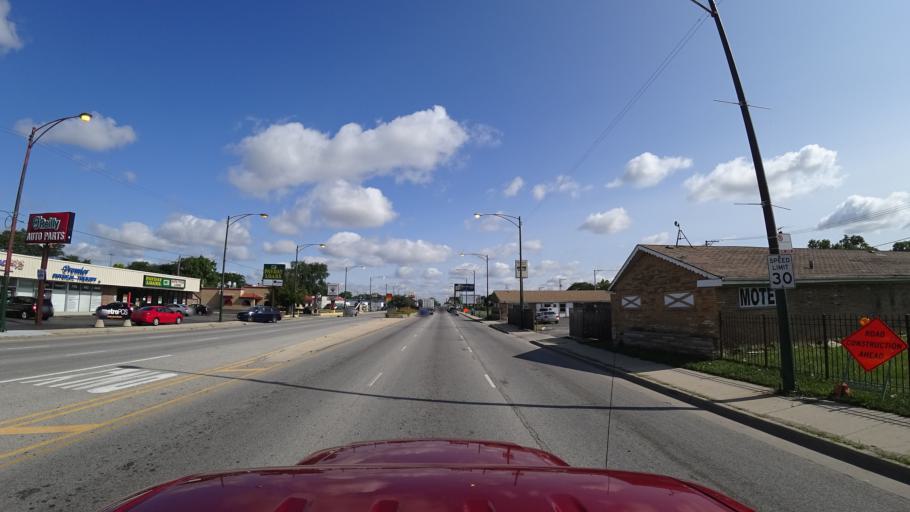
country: US
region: Illinois
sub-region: Cook County
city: Cicero
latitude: 41.8043
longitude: -87.7430
